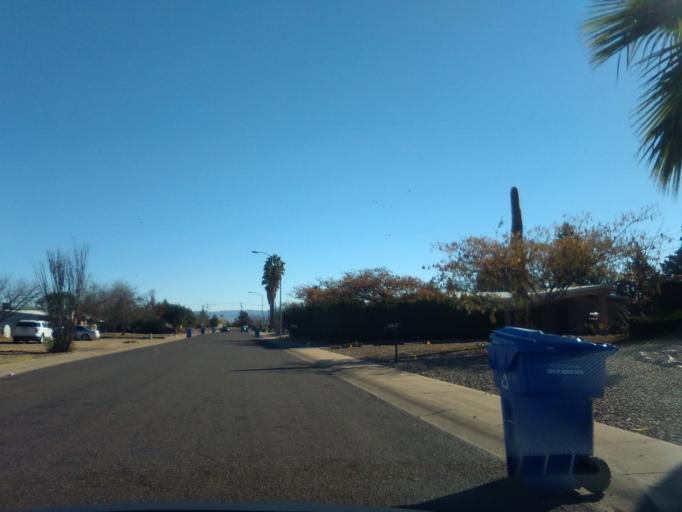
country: US
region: Arizona
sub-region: Cochise County
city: Sierra Vista
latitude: 31.5405
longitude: -110.2776
